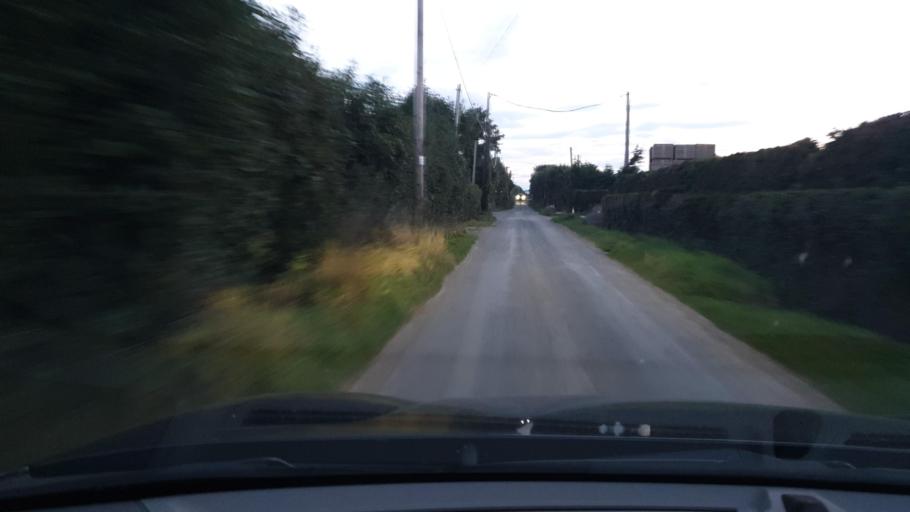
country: IE
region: Leinster
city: An Ros
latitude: 53.5432
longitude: -6.1163
